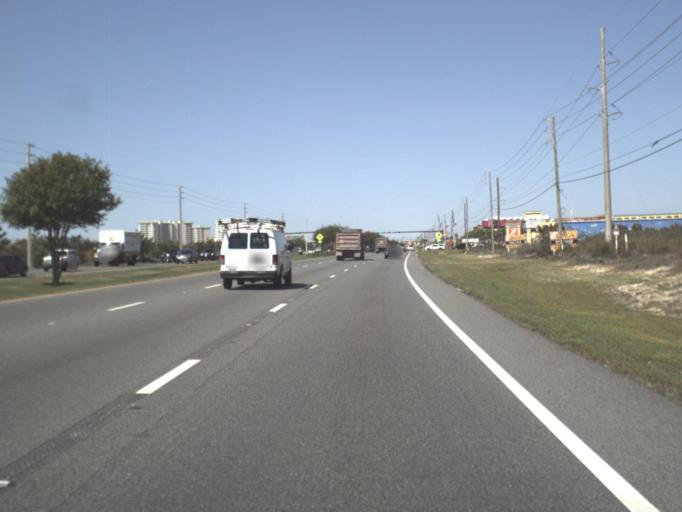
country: US
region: Florida
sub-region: Okaloosa County
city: Destin
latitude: 30.3870
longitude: -86.4402
